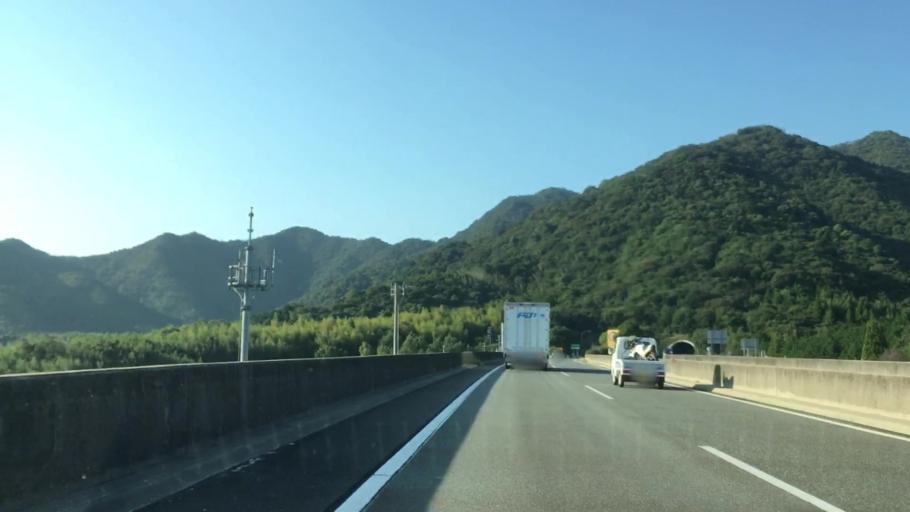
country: JP
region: Yamaguchi
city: Ogori-shimogo
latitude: 34.0976
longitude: 131.4524
